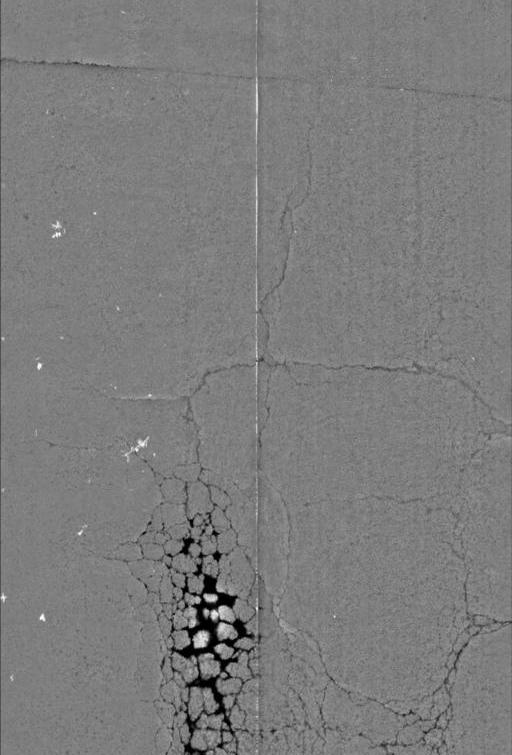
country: US
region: Maryland
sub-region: Prince George's County
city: Chillum
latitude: 38.9440
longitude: -77.0143
